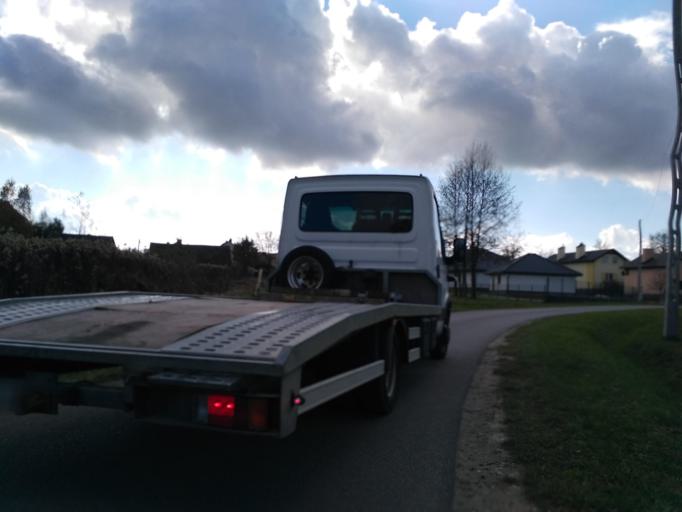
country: PL
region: Subcarpathian Voivodeship
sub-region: Powiat rzeszowski
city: Swilcza
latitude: 50.1198
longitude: 21.8880
